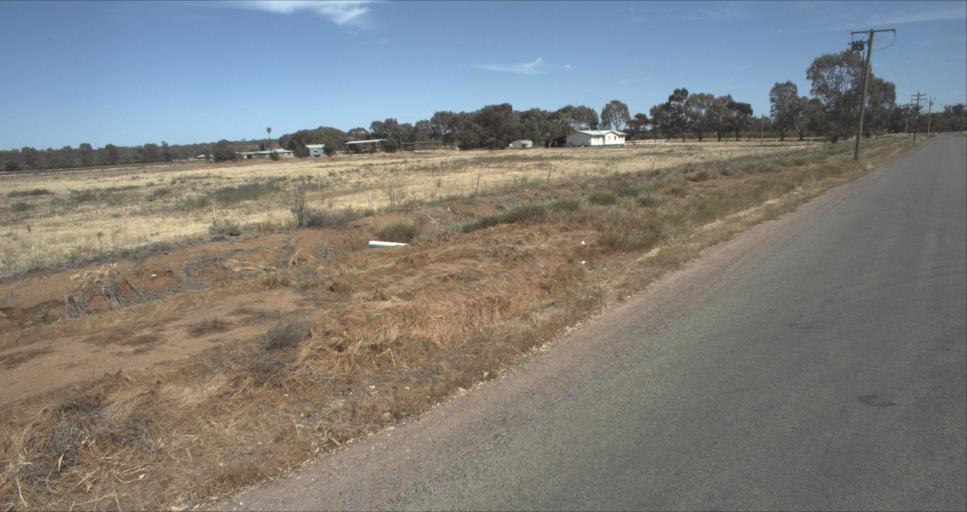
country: AU
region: New South Wales
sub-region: Leeton
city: Leeton
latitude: -34.5796
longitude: 146.4686
